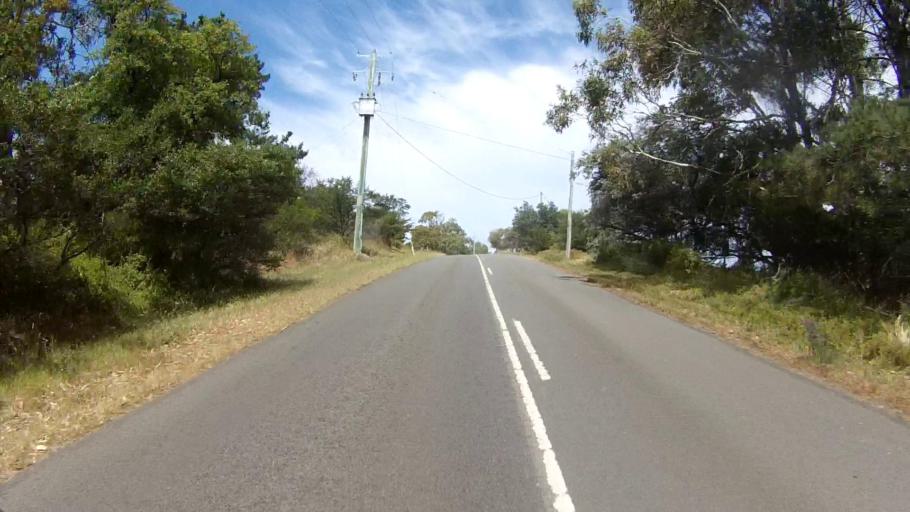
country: AU
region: Tasmania
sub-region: Kingborough
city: Taroona
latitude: -43.0146
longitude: 147.4151
